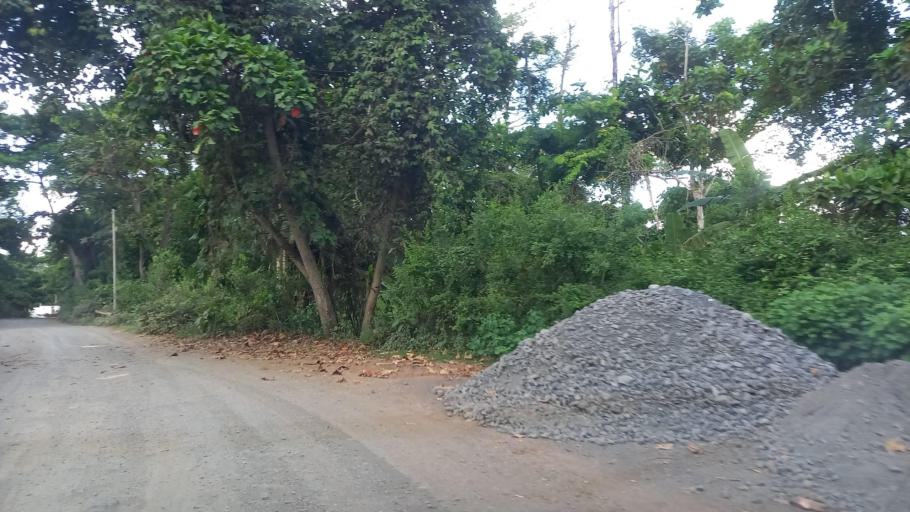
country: YT
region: Dembeni
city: Dembeni
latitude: -12.8296
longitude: 45.1914
